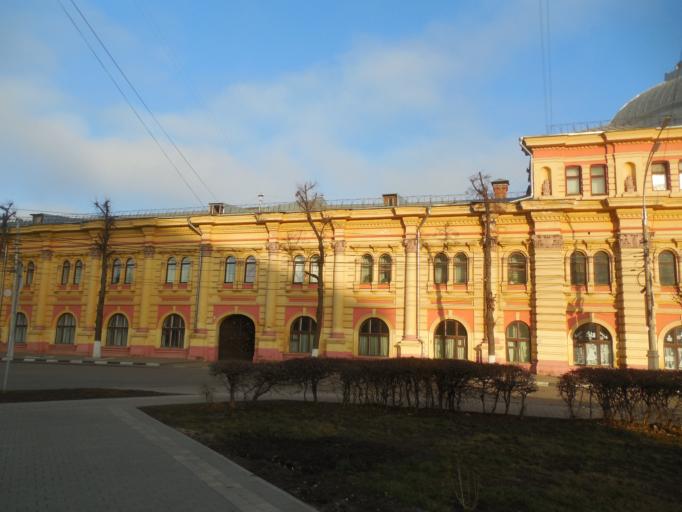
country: RU
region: Tula
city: Tula
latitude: 54.1946
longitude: 37.6157
